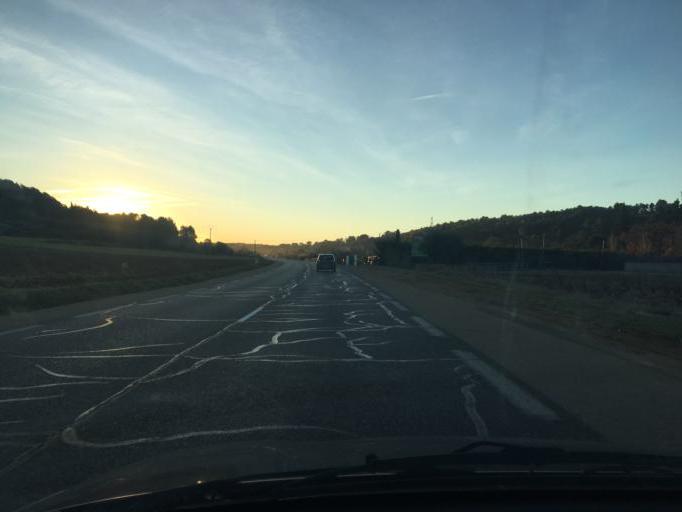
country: FR
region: Provence-Alpes-Cote d'Azur
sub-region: Departement du Var
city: Lorgues
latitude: 43.4758
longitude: 6.3750
